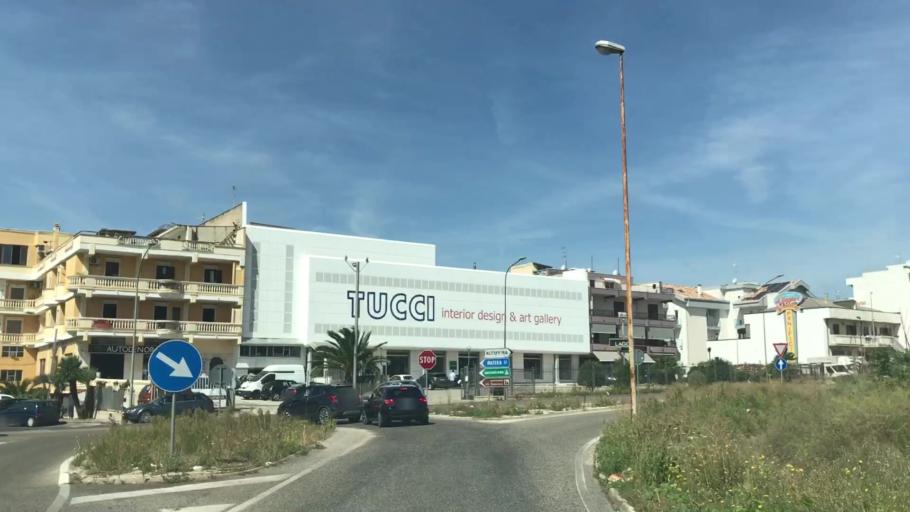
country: IT
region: Apulia
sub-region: Provincia di Bari
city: Altamura
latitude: 40.8160
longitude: 16.5544
